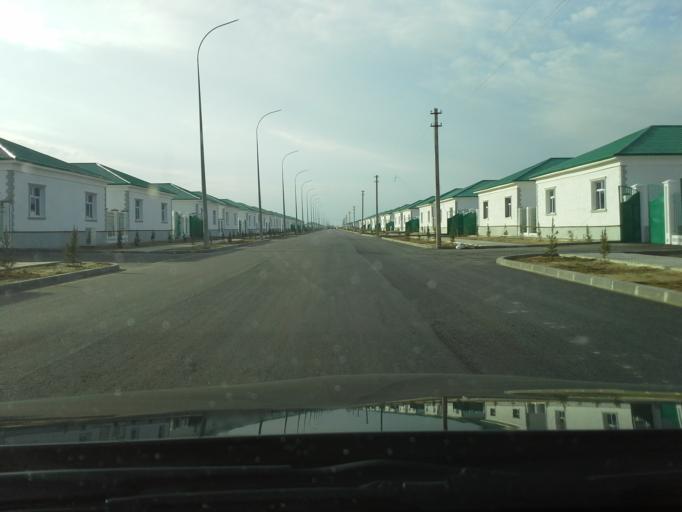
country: TM
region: Ahal
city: Abadan
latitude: 38.0968
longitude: 58.3168
